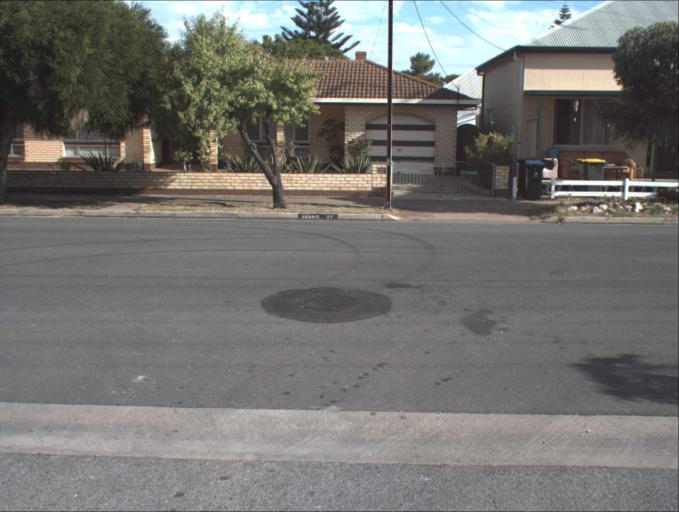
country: AU
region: South Australia
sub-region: Port Adelaide Enfield
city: Birkenhead
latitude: -34.8382
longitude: 138.4902
